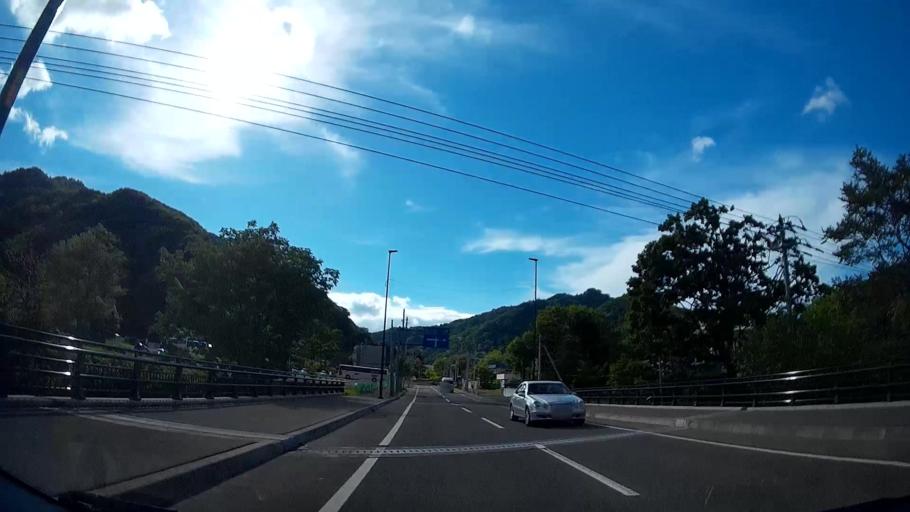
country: JP
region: Hokkaido
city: Sapporo
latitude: 42.9693
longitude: 141.1657
